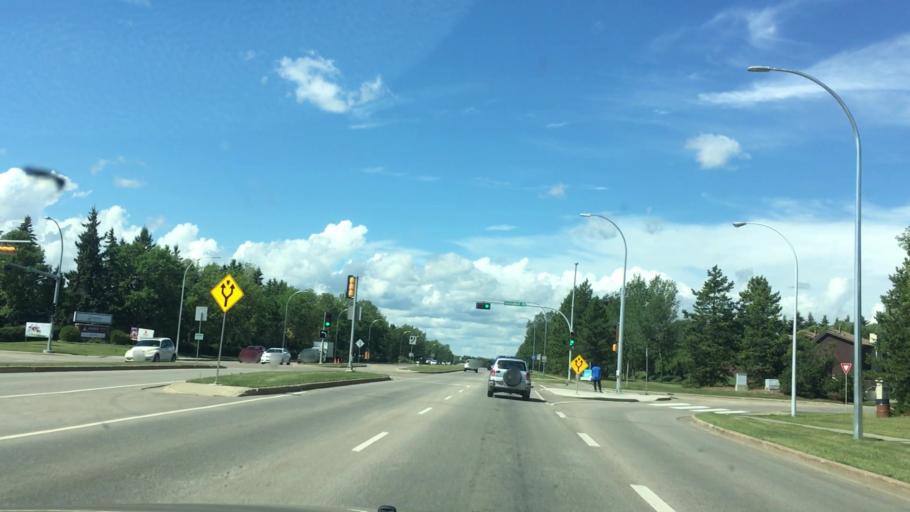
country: CA
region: Alberta
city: Edmonton
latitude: 53.4540
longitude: -113.5246
